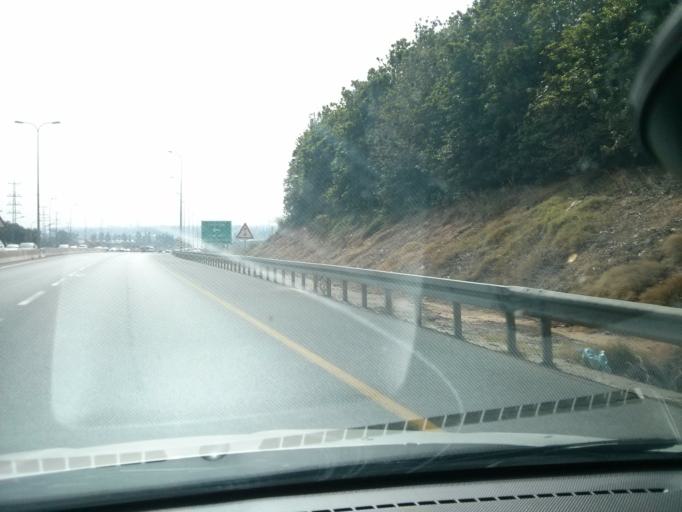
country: IL
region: Central District
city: Even Yehuda
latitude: 32.2554
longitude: 34.8760
